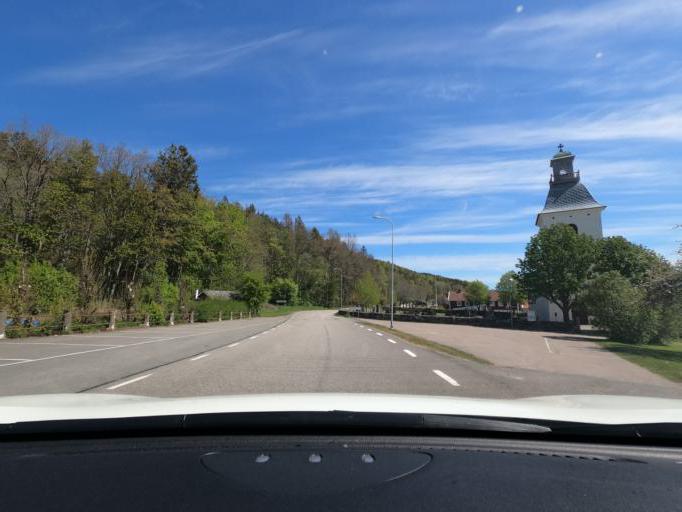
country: SE
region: Vaestra Goetaland
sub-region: Marks Kommun
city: Horred
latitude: 57.4241
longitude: 12.3309
